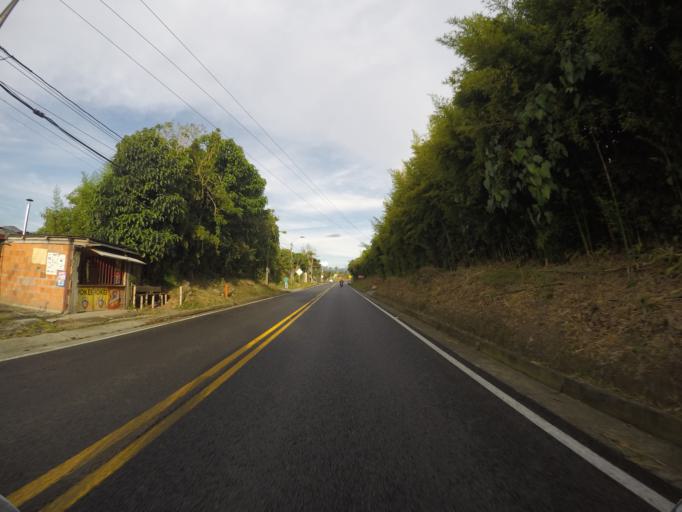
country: CO
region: Risaralda
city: Pereira
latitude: 4.7654
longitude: -75.6886
